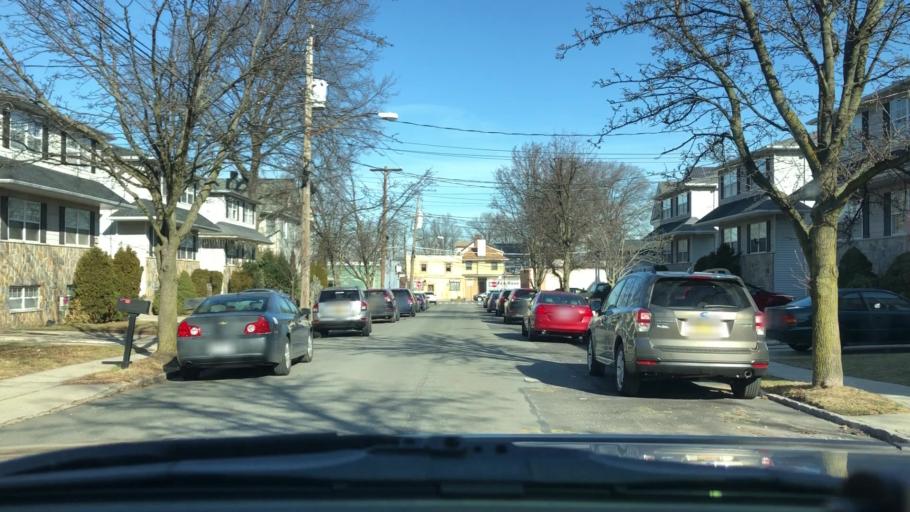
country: US
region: New Jersey
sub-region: Hudson County
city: Bayonne
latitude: 40.6288
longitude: -74.1097
